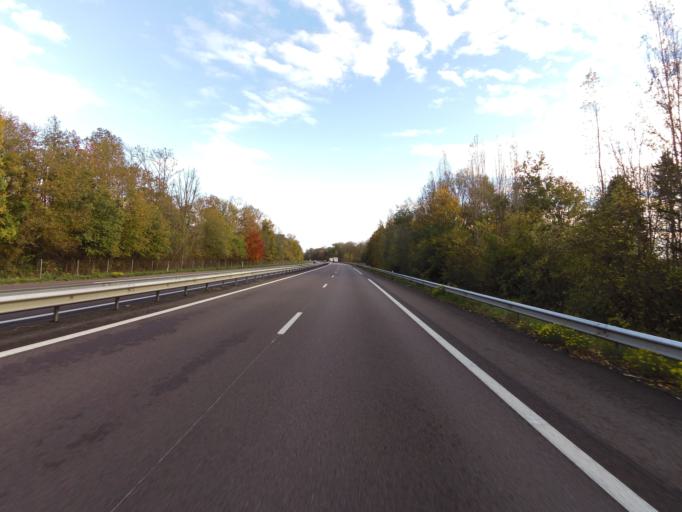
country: FR
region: Bourgogne
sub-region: Departement de la Cote-d'Or
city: Fenay
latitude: 47.2459
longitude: 5.0677
